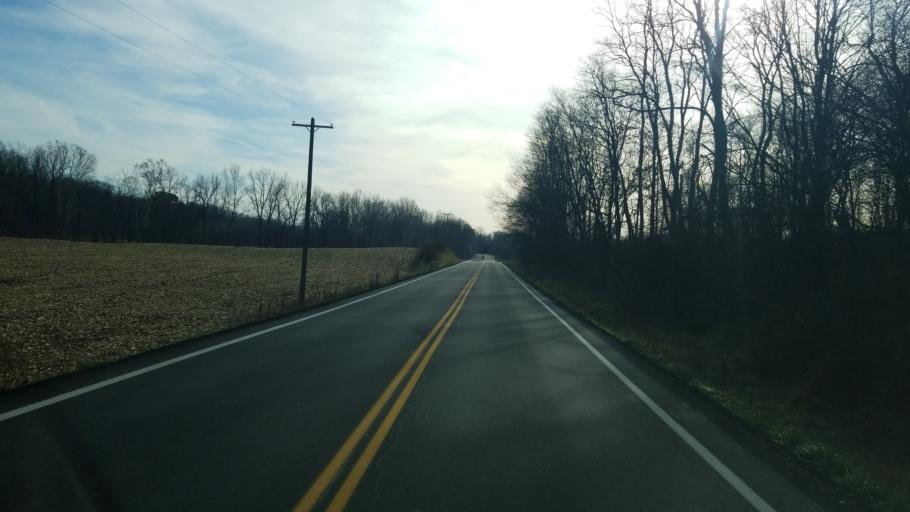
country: US
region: Ohio
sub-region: Ashland County
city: Ashland
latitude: 40.9501
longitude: -82.2635
